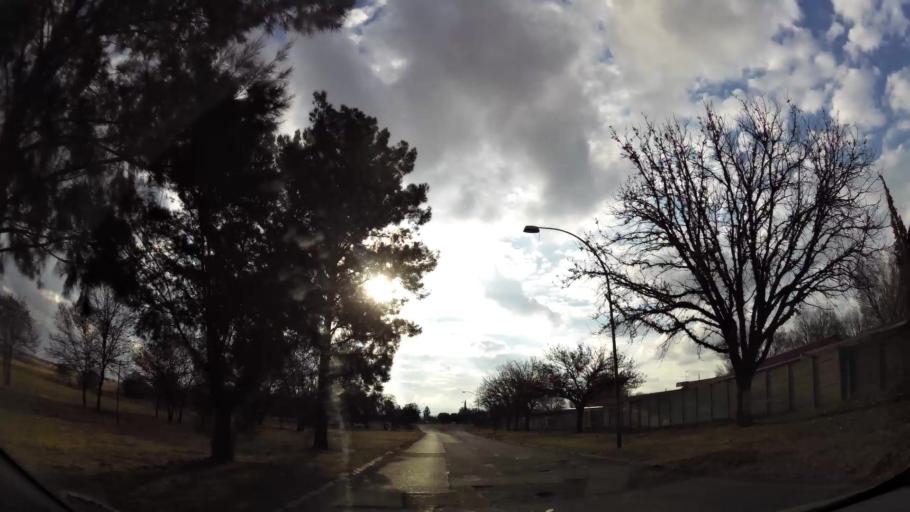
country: ZA
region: Orange Free State
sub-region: Fezile Dabi District Municipality
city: Sasolburg
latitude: -26.8231
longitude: 27.8108
